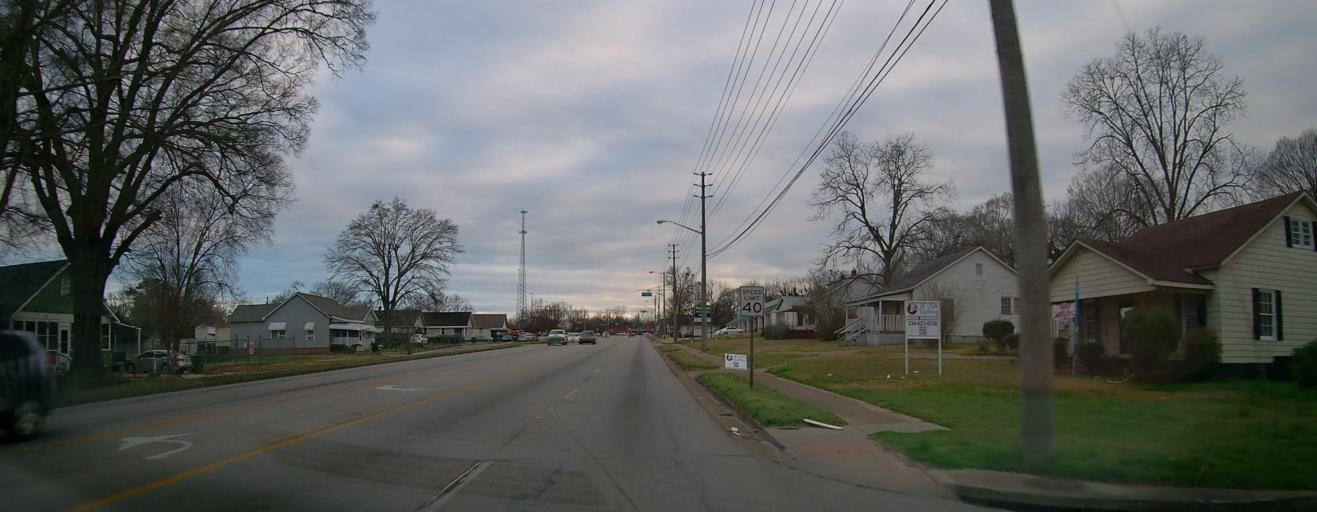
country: US
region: Alabama
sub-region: Chambers County
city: Lanett
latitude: 32.8583
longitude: -85.1912
